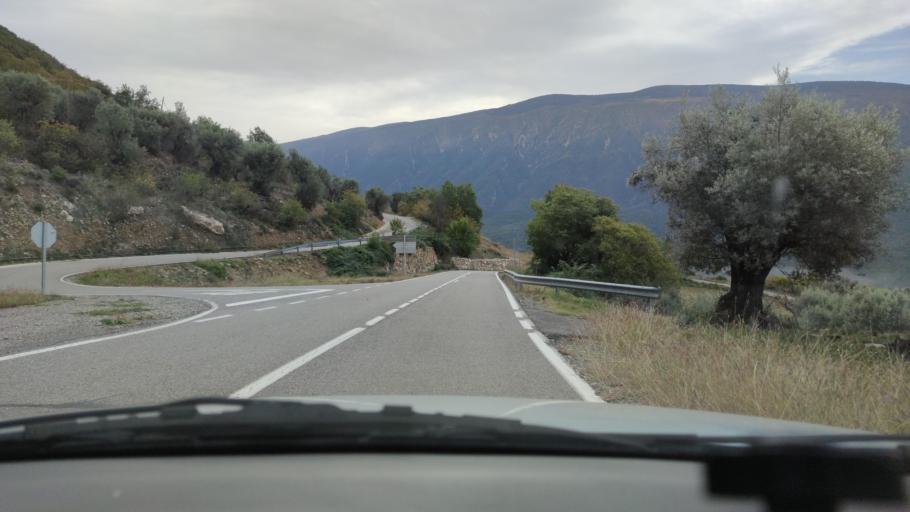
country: ES
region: Catalonia
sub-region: Provincia de Lleida
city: Llimiana
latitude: 42.0696
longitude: 0.9192
